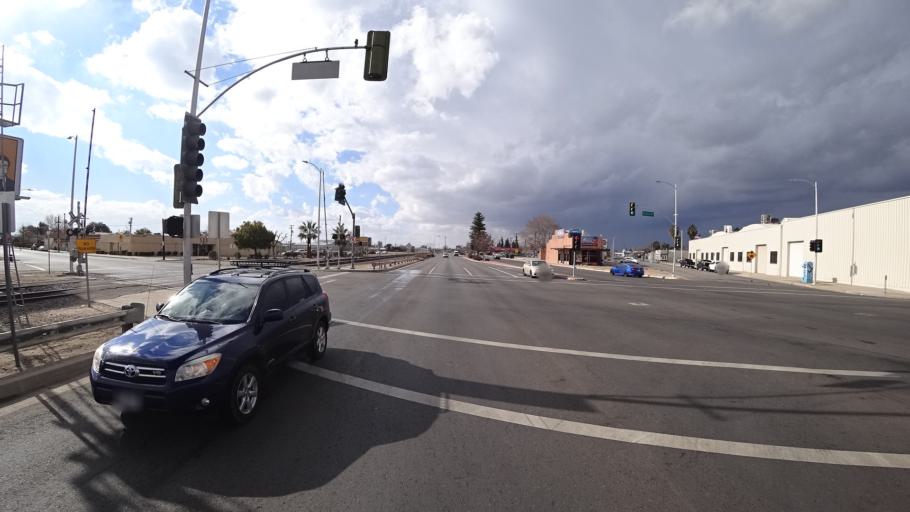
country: US
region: California
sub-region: Kern County
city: Bakersfield
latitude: 35.3736
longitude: -118.9940
